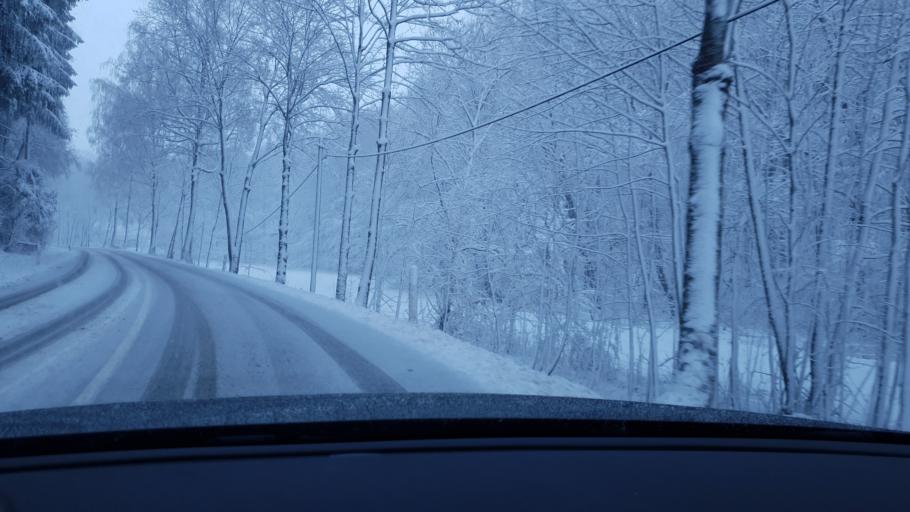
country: DE
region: Saxony
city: Claussnitz
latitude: 50.9047
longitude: 12.8994
